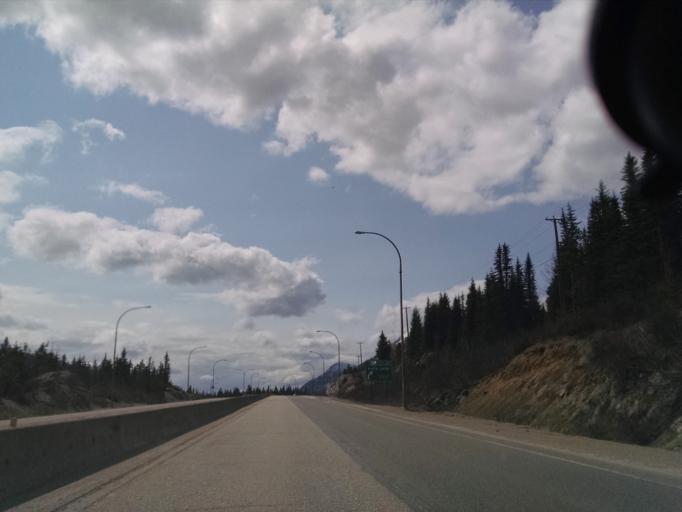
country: CA
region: British Columbia
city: Hope
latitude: 49.6142
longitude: -121.0482
